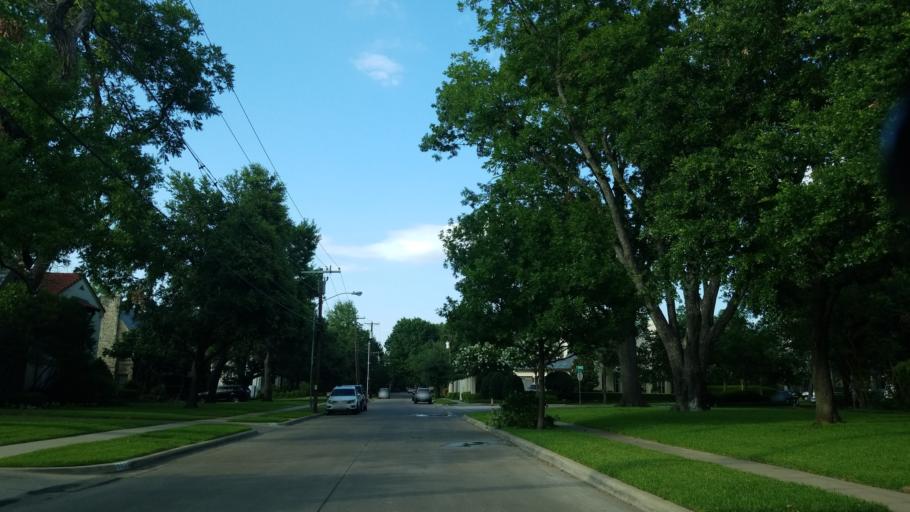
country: US
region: Texas
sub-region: Dallas County
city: University Park
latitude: 32.8470
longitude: -96.7953
